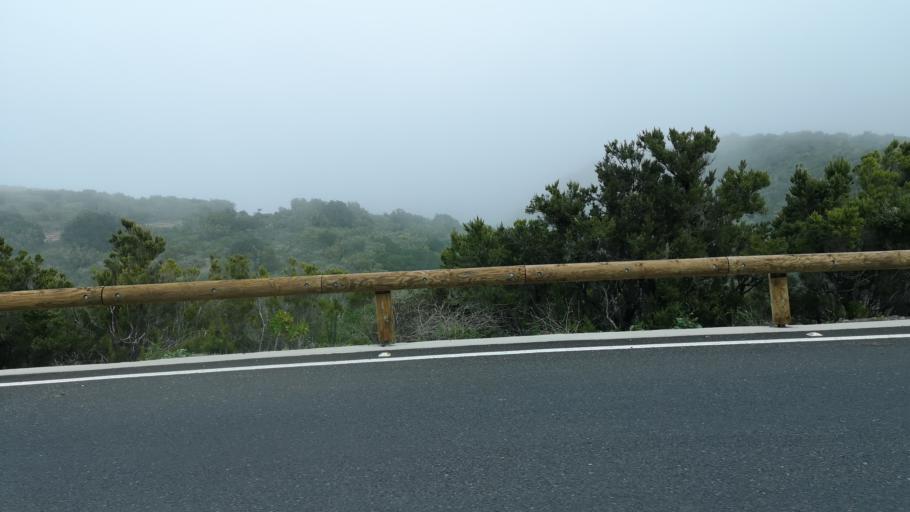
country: ES
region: Canary Islands
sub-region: Provincia de Santa Cruz de Tenerife
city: Vallehermosa
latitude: 28.1443
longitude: -17.3089
